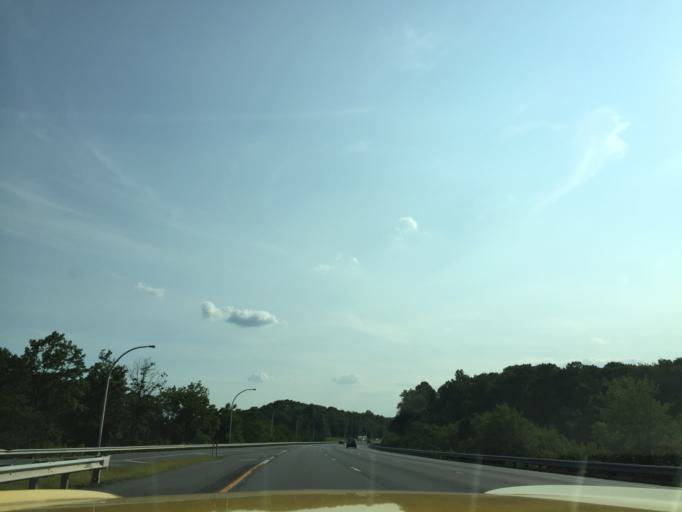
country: US
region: Maryland
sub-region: Cecil County
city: Charlestown
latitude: 39.6112
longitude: -76.0125
